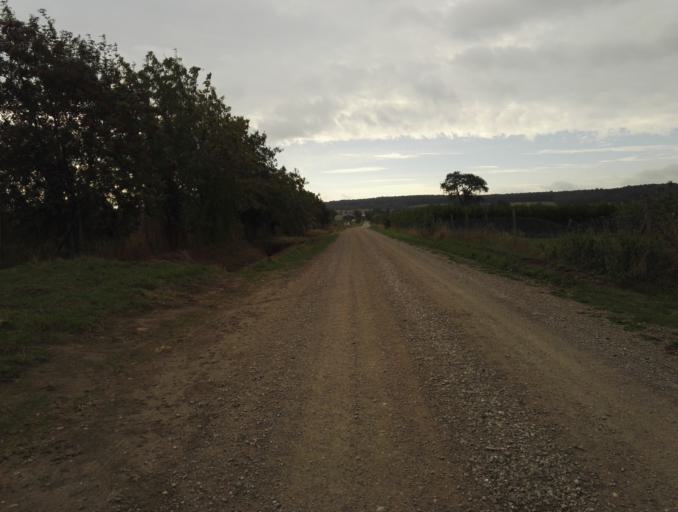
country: DE
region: Lower Saxony
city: Schellerten
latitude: 52.1419
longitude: 10.0644
